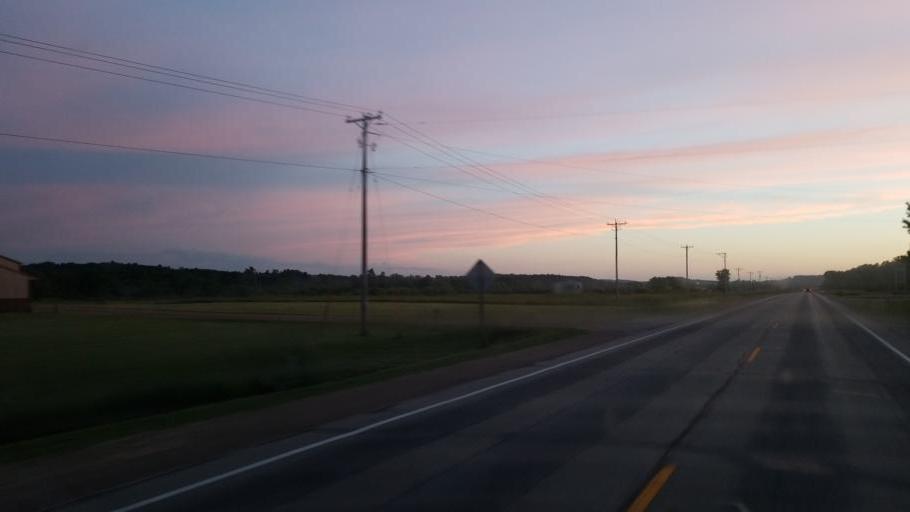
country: US
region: Wisconsin
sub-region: Juneau County
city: Elroy
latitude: 43.6803
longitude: -90.2715
